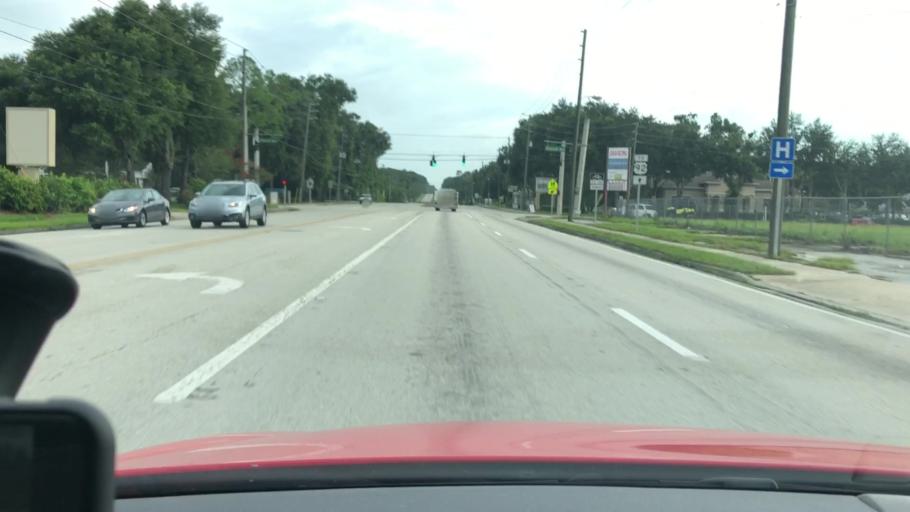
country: US
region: Florida
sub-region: Volusia County
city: DeLand
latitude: 29.0417
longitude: -81.3246
